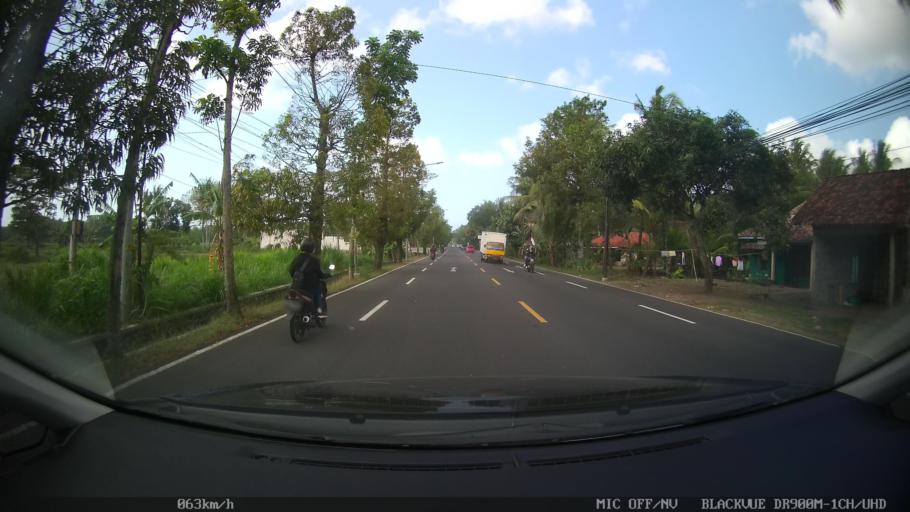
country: ID
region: Daerah Istimewa Yogyakarta
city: Srandakan
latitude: -7.8812
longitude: 110.1320
